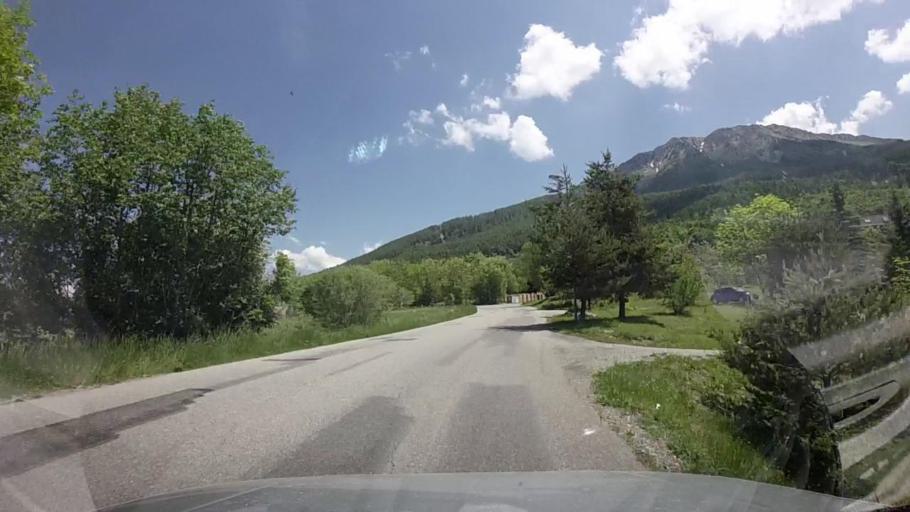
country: FR
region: Provence-Alpes-Cote d'Azur
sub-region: Departement des Alpes-de-Haute-Provence
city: Seyne-les-Alpes
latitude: 44.4133
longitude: 6.3499
